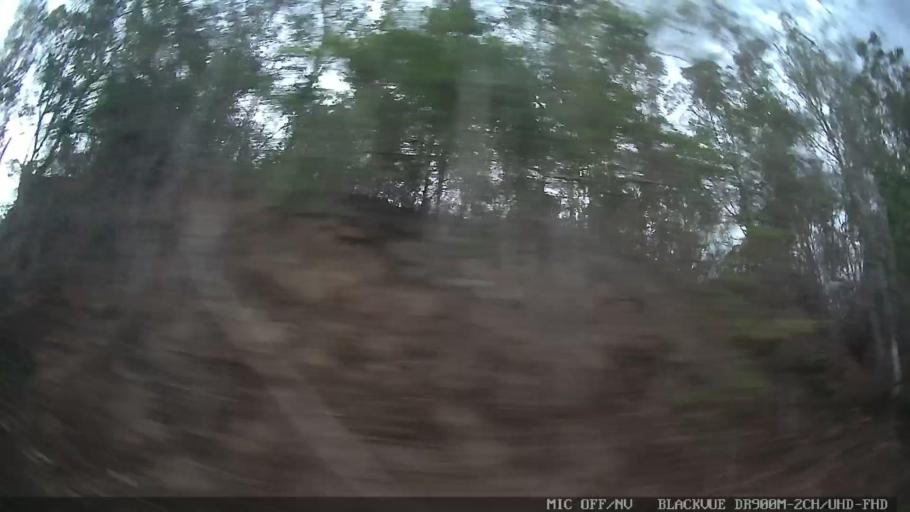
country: BR
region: Sao Paulo
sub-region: Amparo
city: Amparo
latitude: -22.7654
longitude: -46.7574
